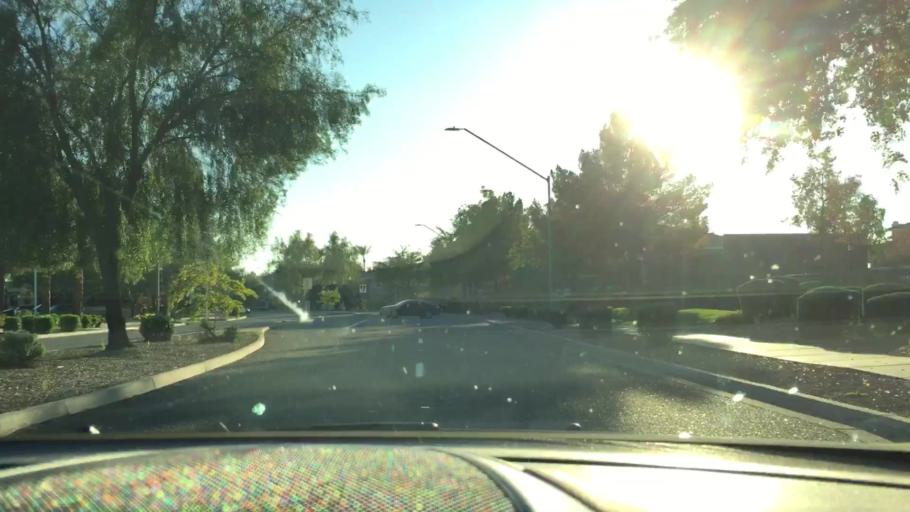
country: US
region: Arizona
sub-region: Maricopa County
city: Sun City
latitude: 33.6516
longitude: -112.2295
